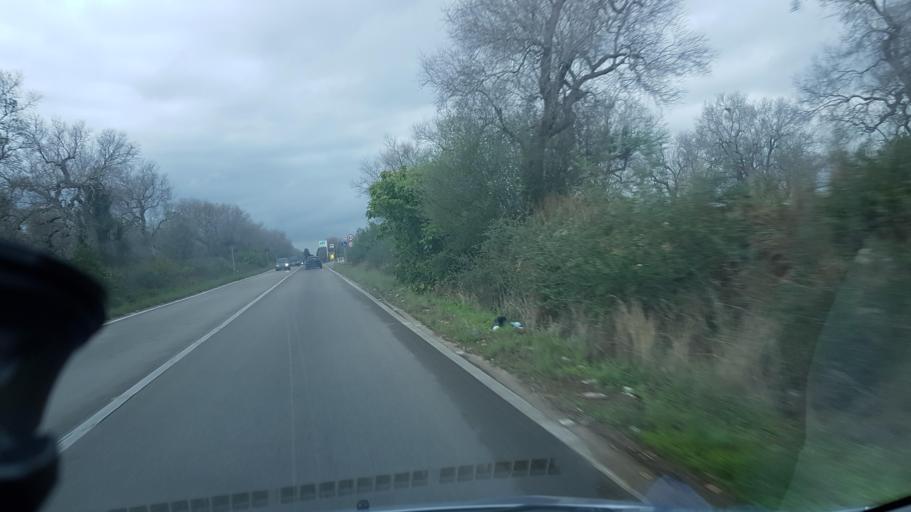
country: IT
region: Apulia
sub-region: Provincia di Lecce
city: Arnesano
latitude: 40.3619
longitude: 18.0931
